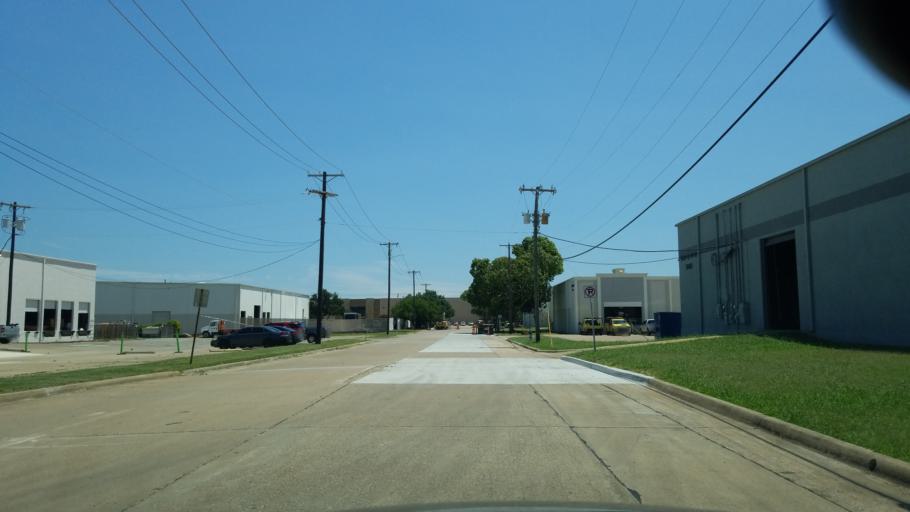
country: US
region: Texas
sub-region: Dallas County
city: Carrollton
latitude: 32.9486
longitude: -96.9141
